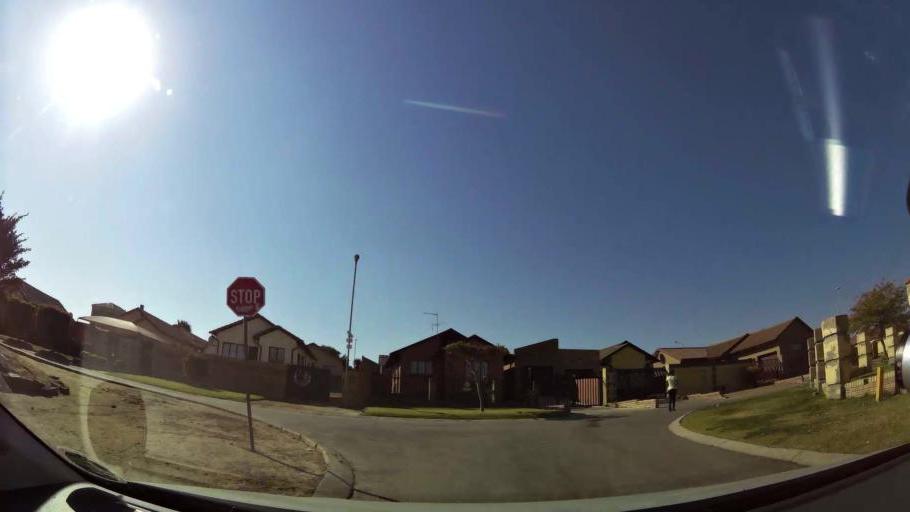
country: ZA
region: Gauteng
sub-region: Ekurhuleni Metropolitan Municipality
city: Tembisa
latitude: -26.0397
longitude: 28.1935
